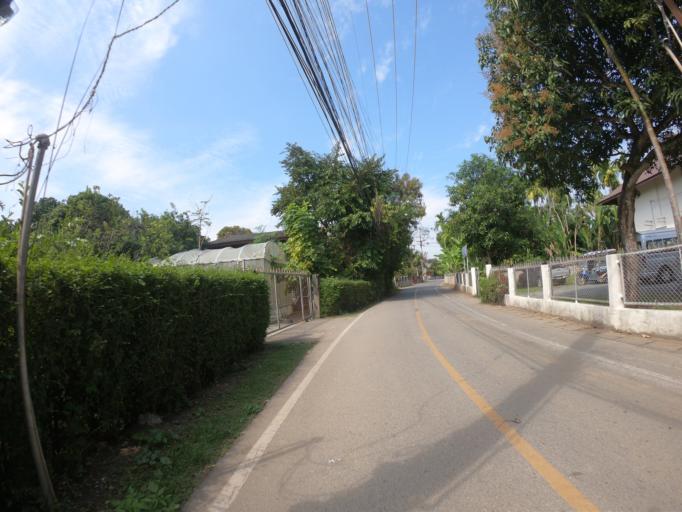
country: TH
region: Chiang Mai
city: San Sai
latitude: 18.8617
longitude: 99.0599
